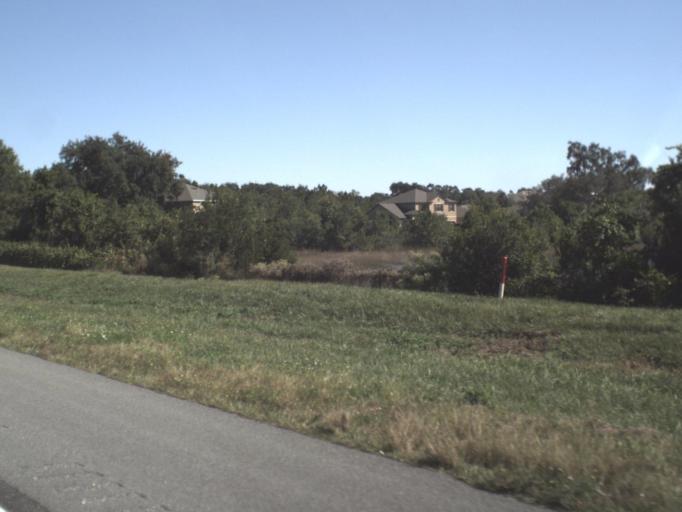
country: US
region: Florida
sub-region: Pasco County
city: Shady Hills
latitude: 28.3456
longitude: -82.5477
